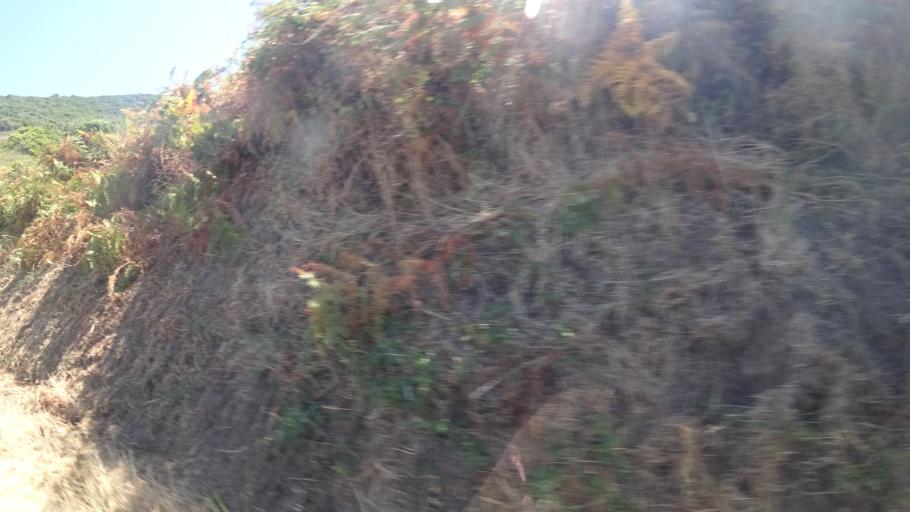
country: FR
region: Corsica
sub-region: Departement de la Corse-du-Sud
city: Alata
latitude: 41.9802
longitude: 8.6750
